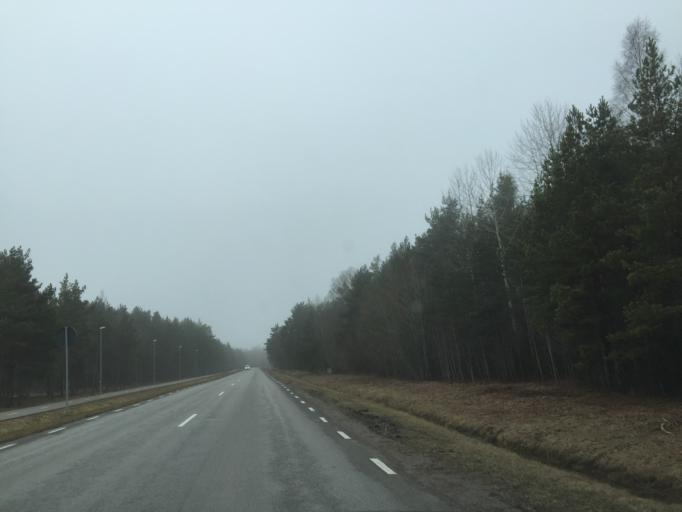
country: EE
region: Saare
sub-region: Kuressaare linn
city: Kuressaare
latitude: 58.2451
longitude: 22.4547
